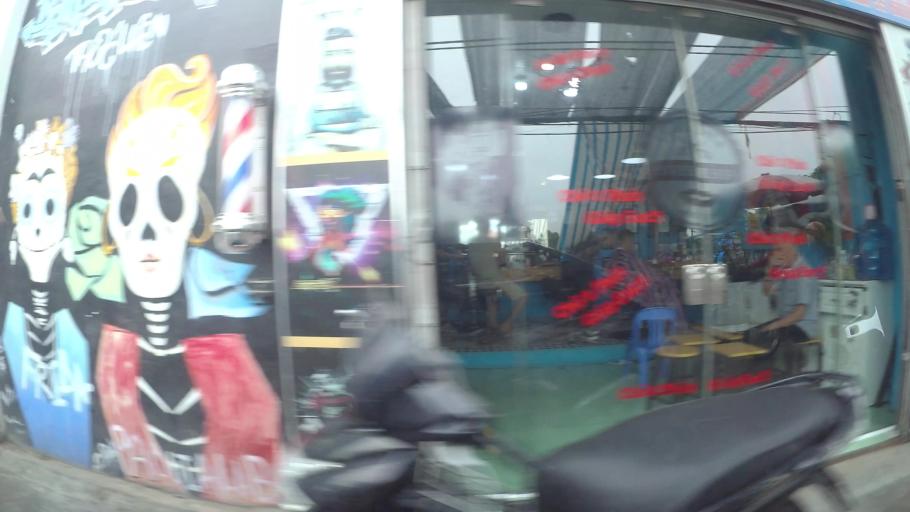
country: VN
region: Ha Noi
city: Hai BaTrung
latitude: 20.9881
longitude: 105.8885
